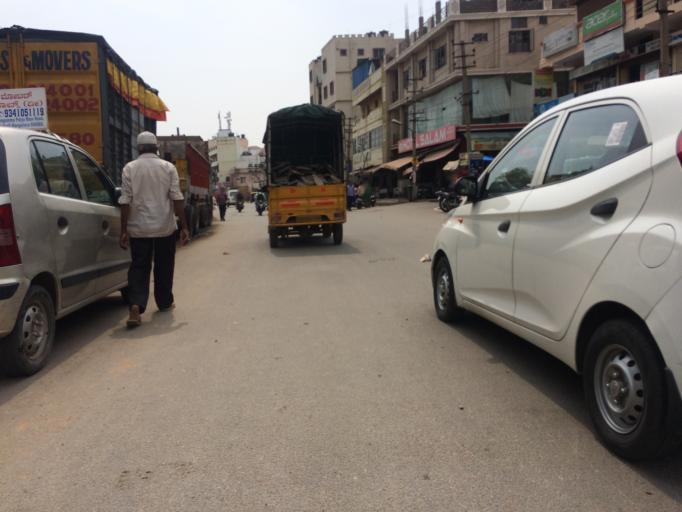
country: IN
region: Karnataka
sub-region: Bangalore Urban
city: Bangalore
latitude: 12.9067
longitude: 77.6330
